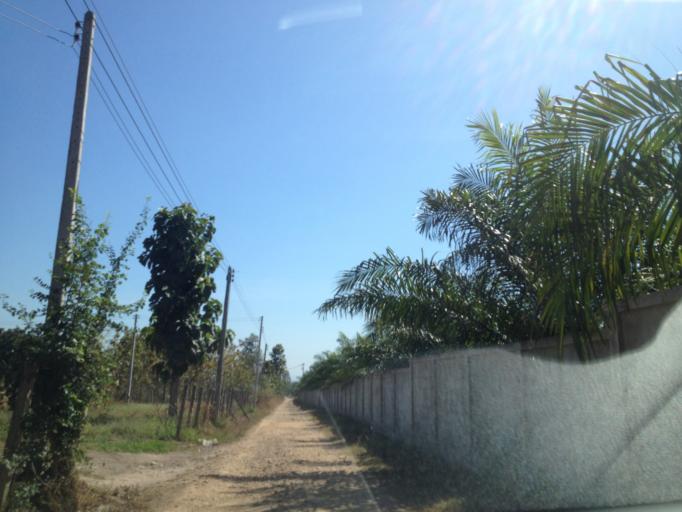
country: TH
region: Chiang Mai
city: San Pa Tong
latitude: 18.6724
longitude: 98.8687
